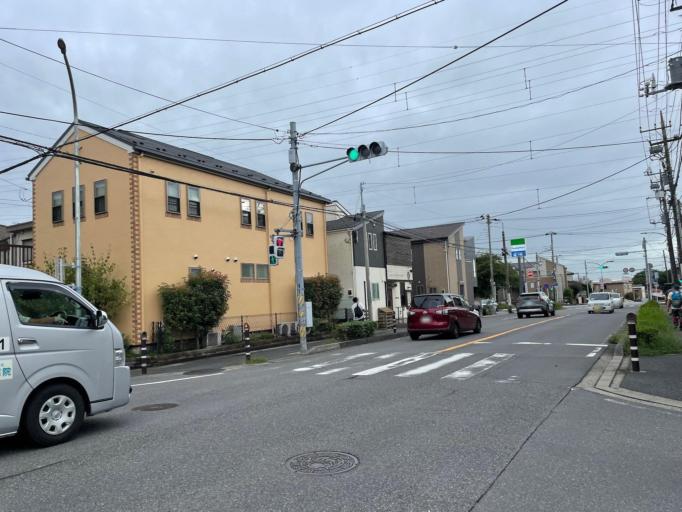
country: JP
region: Chiba
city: Chiba
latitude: 35.6558
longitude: 140.0684
